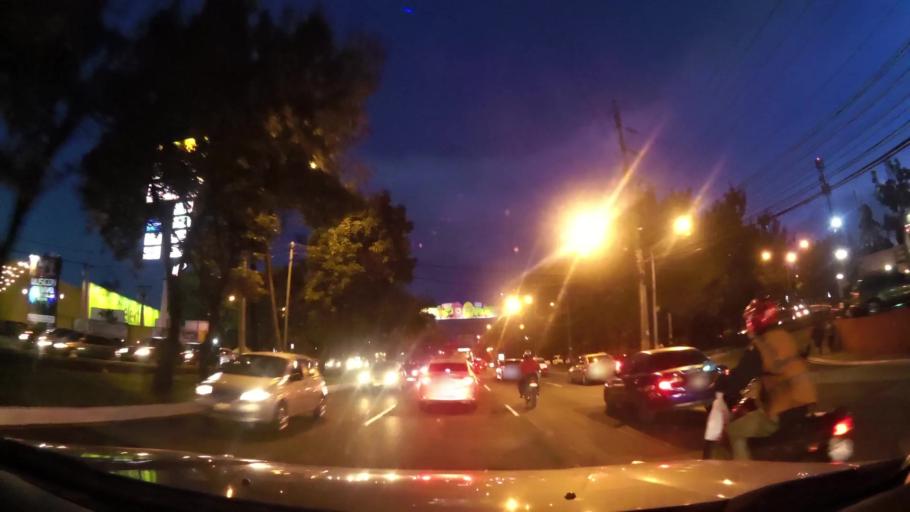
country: GT
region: Guatemala
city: Mixco
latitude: 14.6270
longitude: -90.5593
